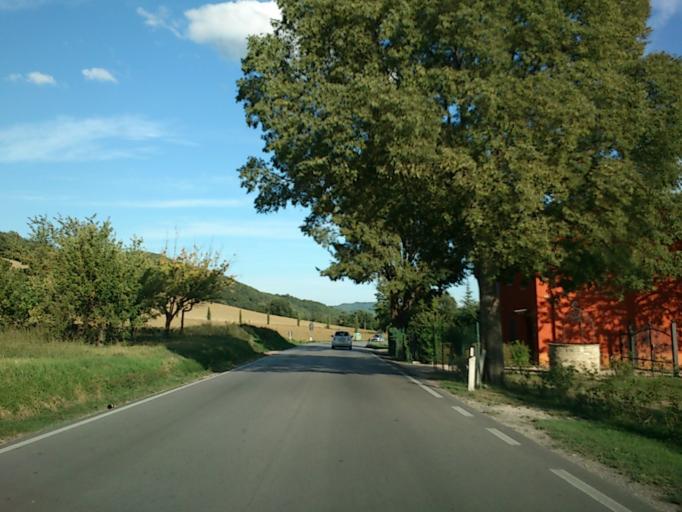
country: IT
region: The Marches
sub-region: Provincia di Pesaro e Urbino
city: Urbania
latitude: 43.6551
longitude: 12.5466
